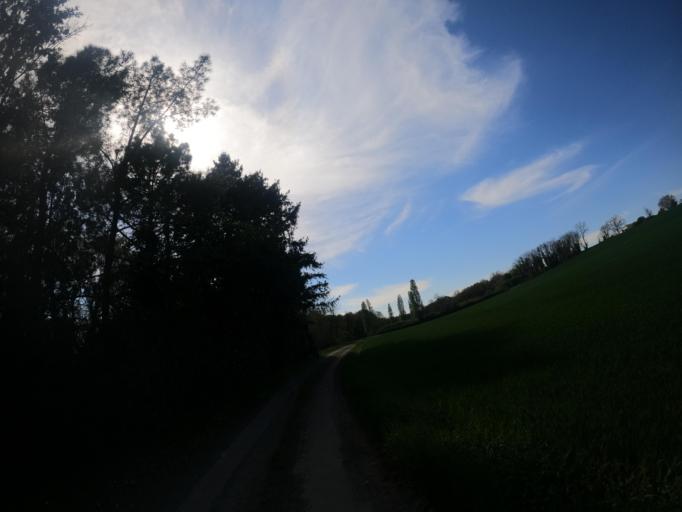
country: FR
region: Poitou-Charentes
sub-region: Departement des Deux-Sevres
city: Saint-Varent
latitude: 46.9161
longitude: -0.1984
